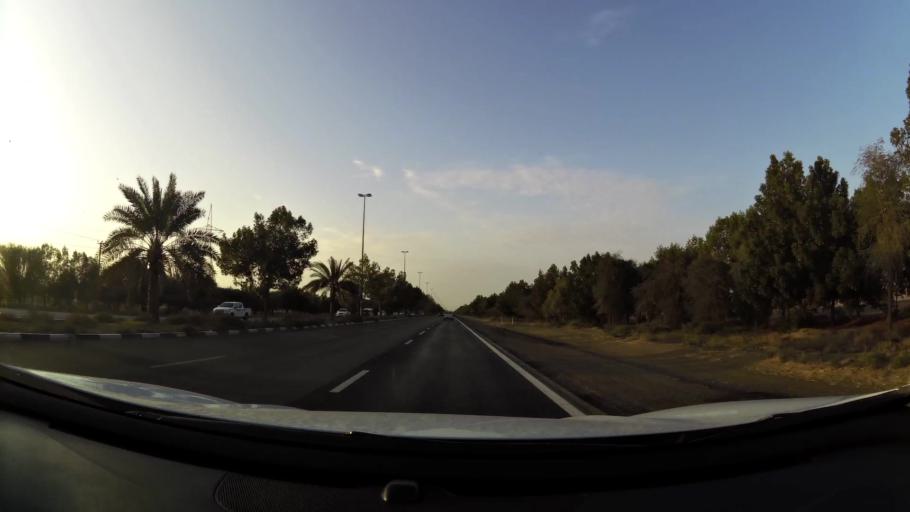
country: AE
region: Abu Dhabi
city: Al Ain
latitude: 24.1705
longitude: 55.8000
